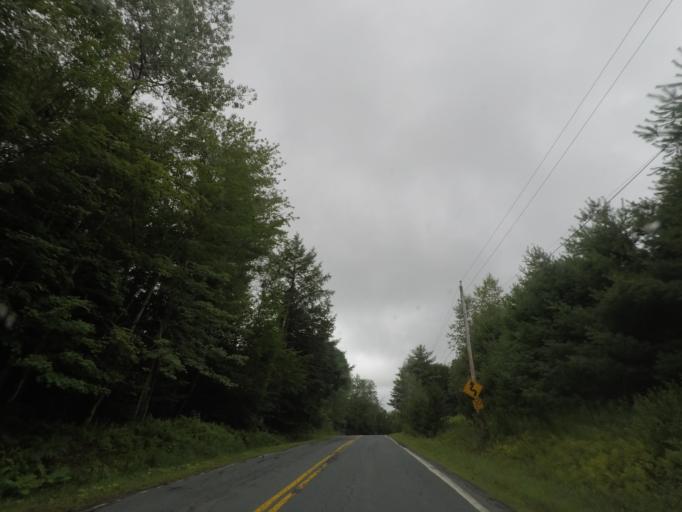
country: US
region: New York
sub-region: Rensselaer County
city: Poestenkill
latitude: 42.6899
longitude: -73.4464
